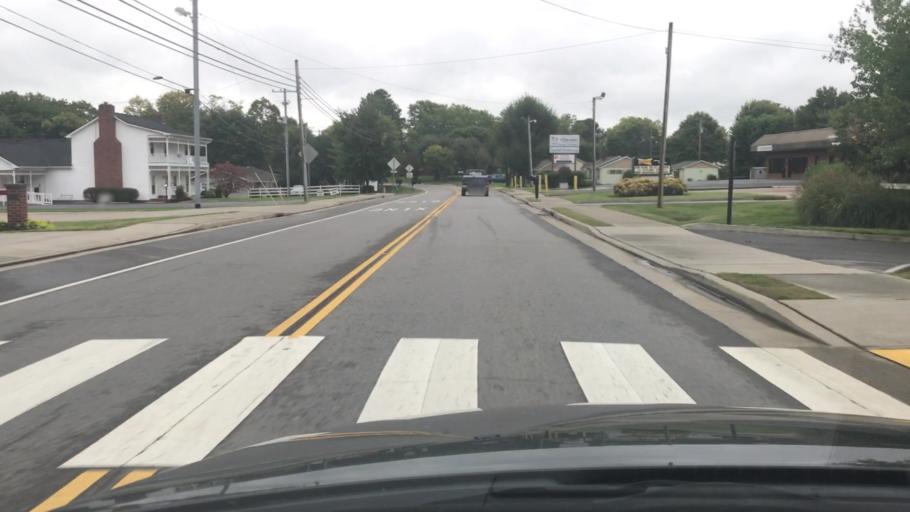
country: US
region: Tennessee
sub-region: Sumner County
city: White House
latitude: 36.4685
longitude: -86.6621
